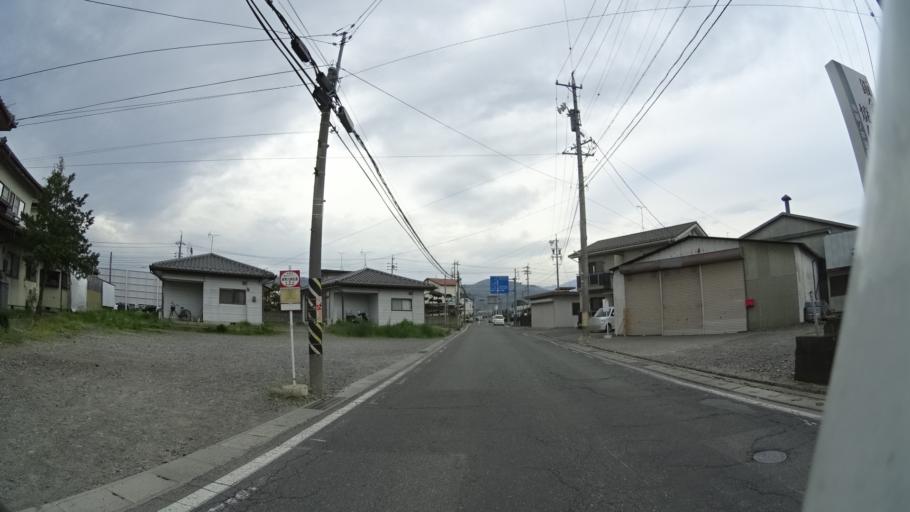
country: JP
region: Nagano
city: Nagano-shi
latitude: 36.5687
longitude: 138.1424
